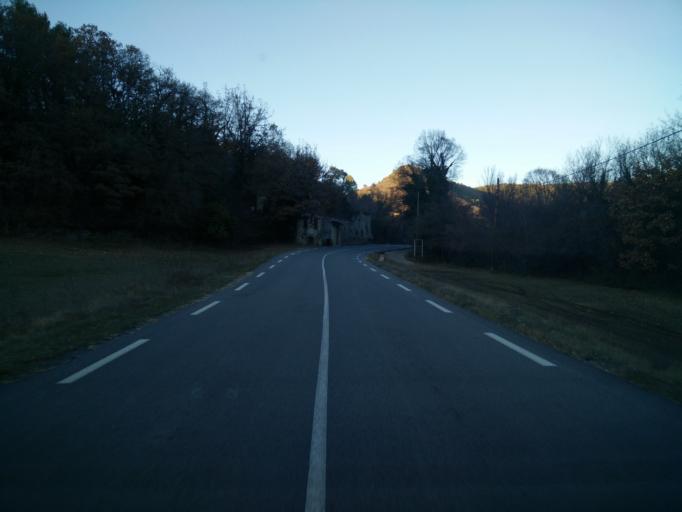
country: FR
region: Provence-Alpes-Cote d'Azur
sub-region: Departement du Var
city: Montferrat
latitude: 43.6066
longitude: 6.4807
